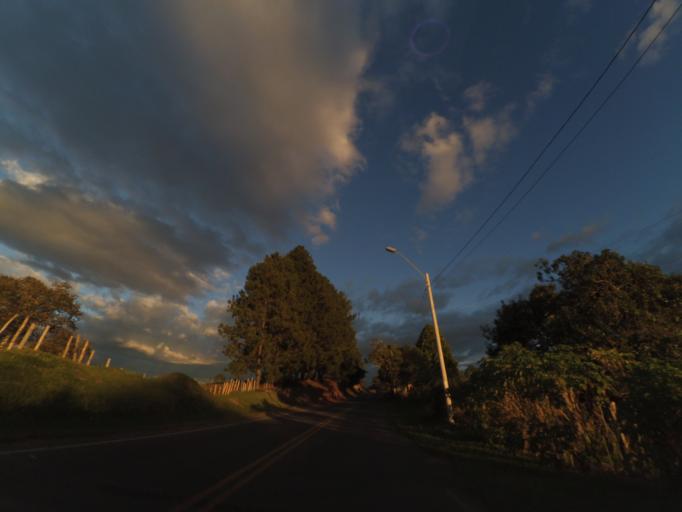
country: CO
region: Cauca
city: Popayan
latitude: 2.4725
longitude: -76.6583
